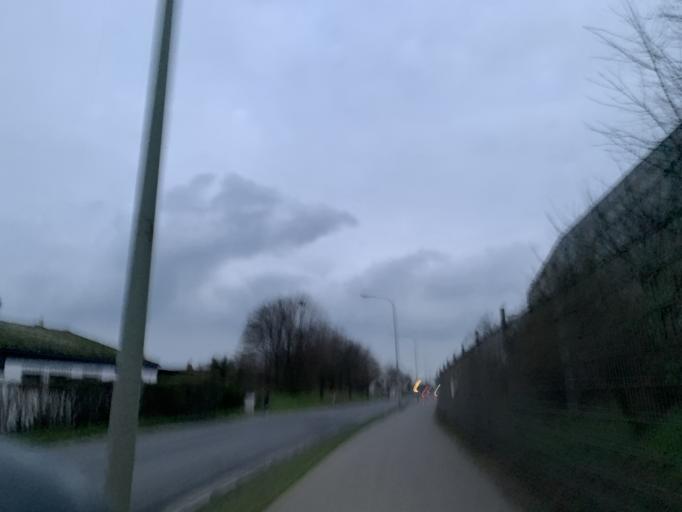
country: DE
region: North Rhine-Westphalia
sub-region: Regierungsbezirk Dusseldorf
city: Meerbusch
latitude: 51.3416
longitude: 6.6794
